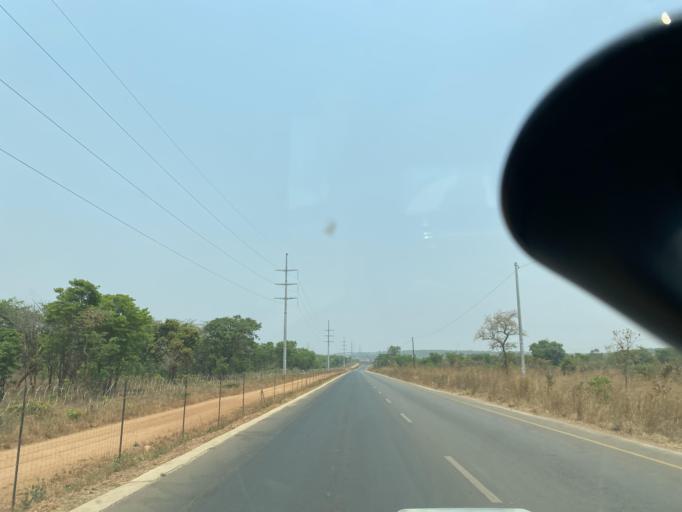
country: ZM
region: Lusaka
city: Lusaka
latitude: -15.5347
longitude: 28.4697
